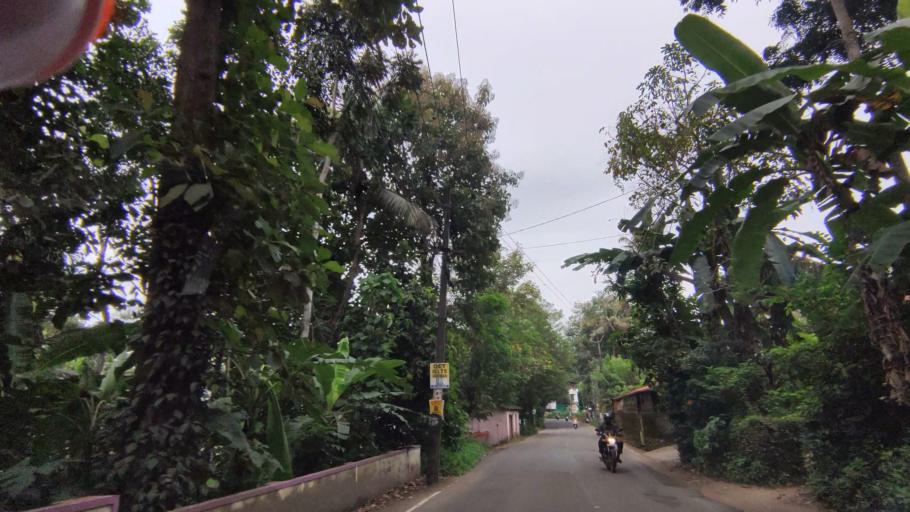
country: IN
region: Kerala
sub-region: Kottayam
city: Kottayam
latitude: 9.6612
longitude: 76.5298
